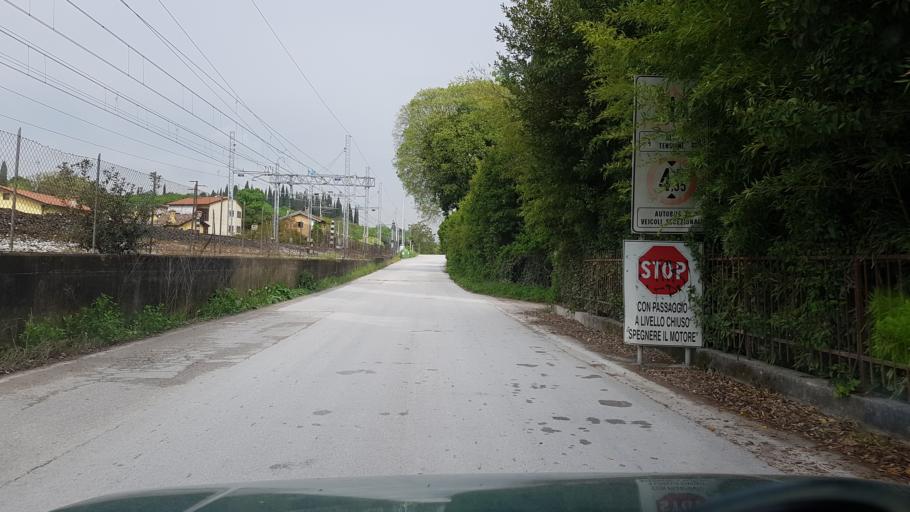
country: IT
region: Friuli Venezia Giulia
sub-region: Provincia di Gorizia
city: Fogliano
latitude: 45.8463
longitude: 13.4904
